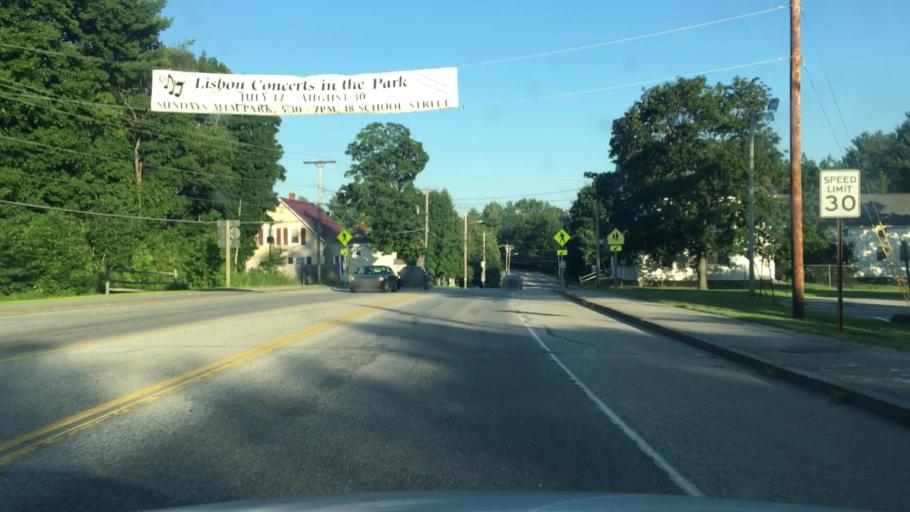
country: US
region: Maine
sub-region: Androscoggin County
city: Lisbon Falls
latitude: 44.0035
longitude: -70.0701
